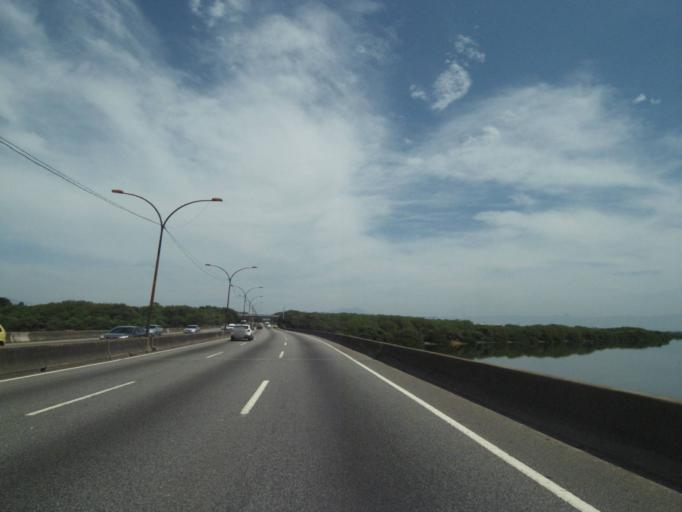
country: BR
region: Rio de Janeiro
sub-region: Duque De Caxias
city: Duque de Caxias
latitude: -22.8105
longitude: -43.2717
